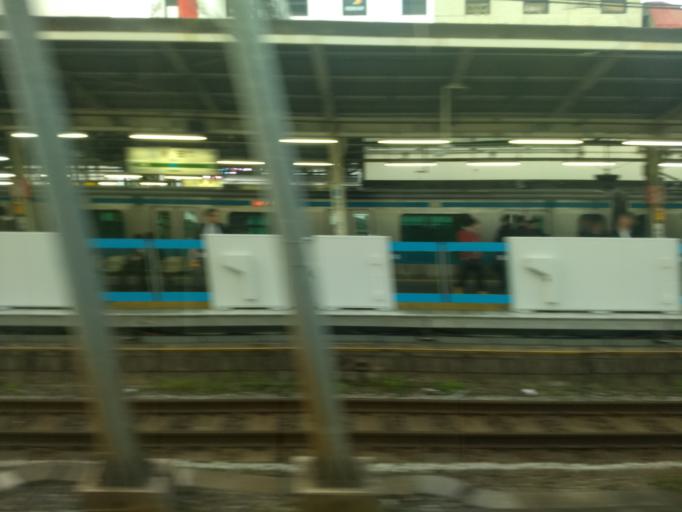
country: JP
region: Kanagawa
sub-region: Kawasaki-shi
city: Kawasaki
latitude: 35.5629
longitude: 139.7163
